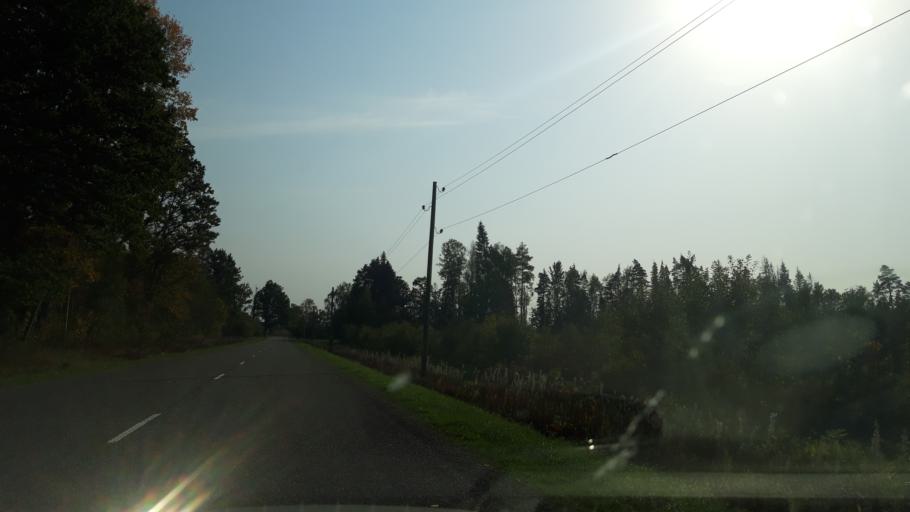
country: LV
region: Burtnieki
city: Matisi
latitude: 57.6288
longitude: 25.2651
